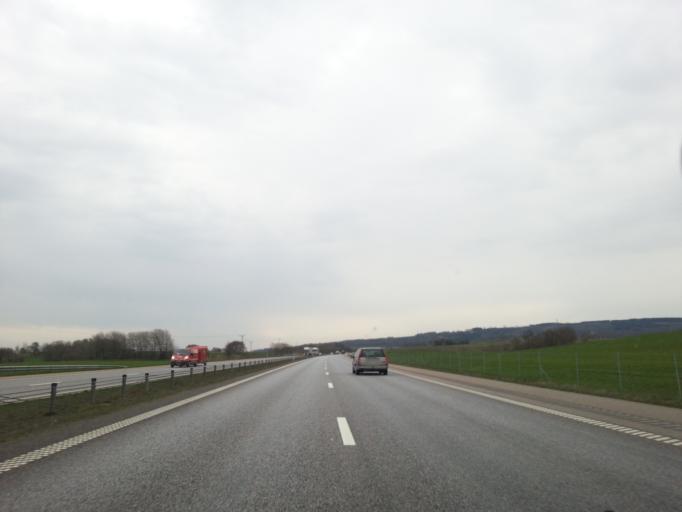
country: SE
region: Halland
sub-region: Halmstads Kommun
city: Getinge
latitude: 56.7837
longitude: 12.7994
